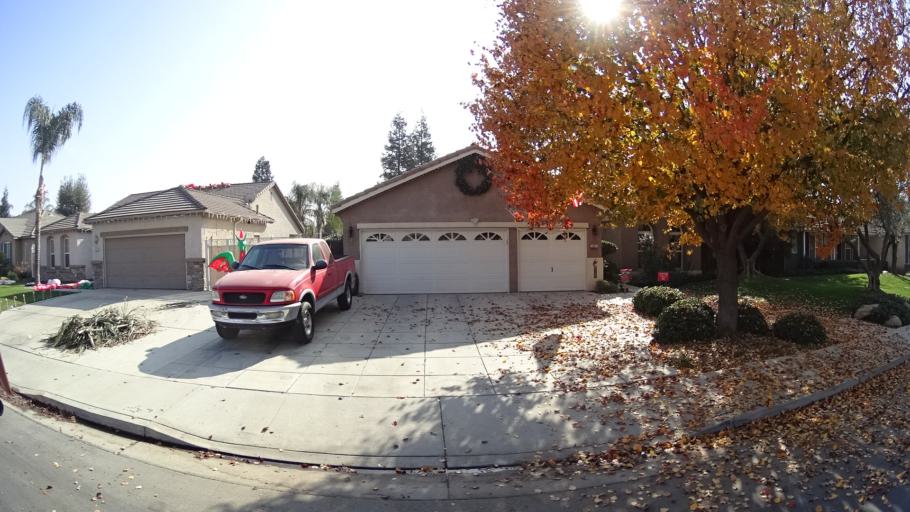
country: US
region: California
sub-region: Kern County
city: Greenacres
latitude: 35.4255
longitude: -119.1178
